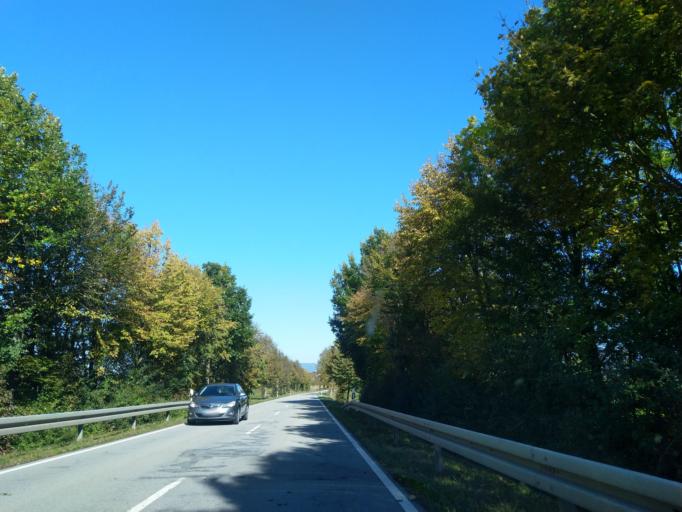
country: DE
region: Bavaria
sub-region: Lower Bavaria
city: Stephansposching
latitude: 48.8073
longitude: 12.8009
